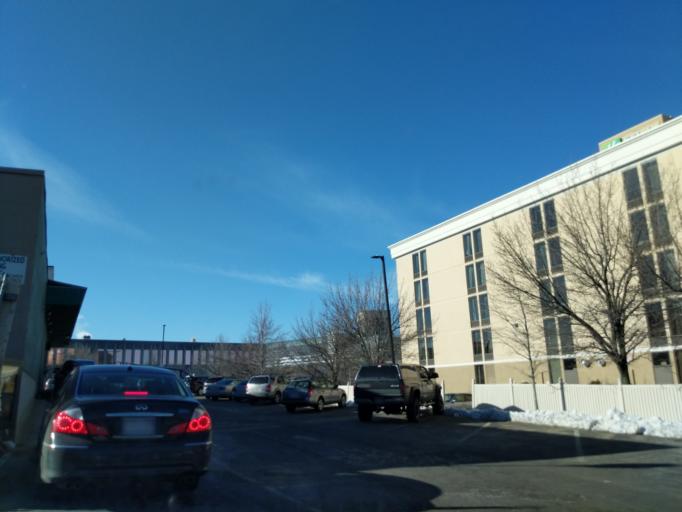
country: US
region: Massachusetts
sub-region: Worcester County
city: Worcester
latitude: 42.2672
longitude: -71.7945
